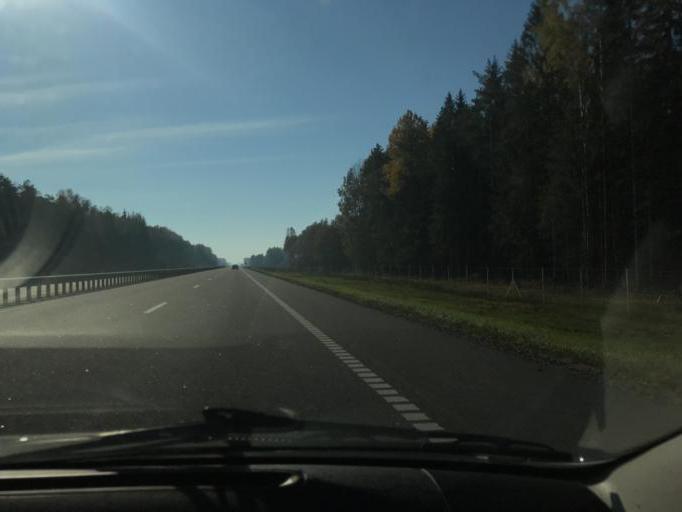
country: BY
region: Minsk
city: Slutsk
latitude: 53.2623
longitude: 27.5501
